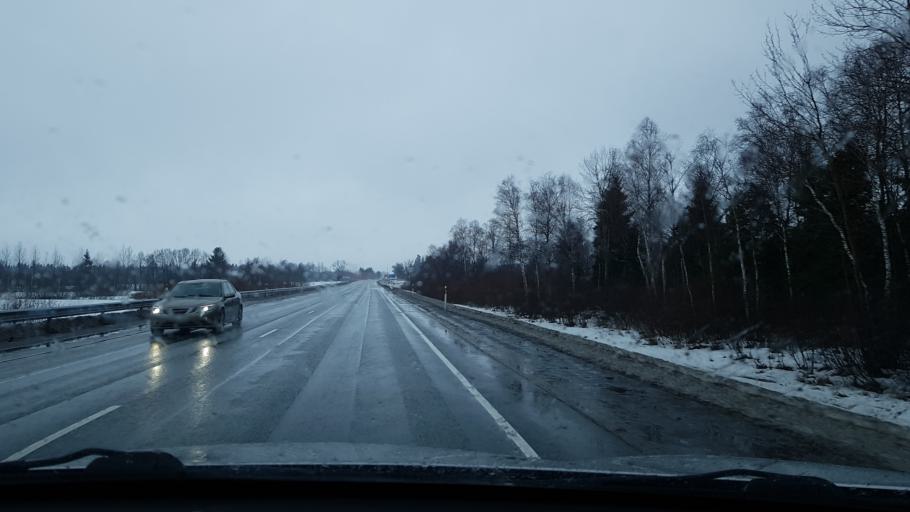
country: EE
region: Raplamaa
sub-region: Kohila vald
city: Kohila
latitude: 59.1965
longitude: 24.7857
